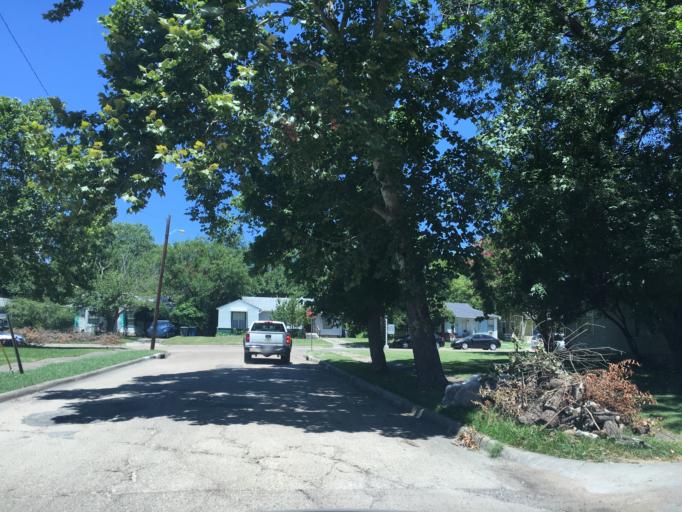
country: US
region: Texas
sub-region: Dallas County
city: Garland
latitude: 32.8447
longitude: -96.6769
